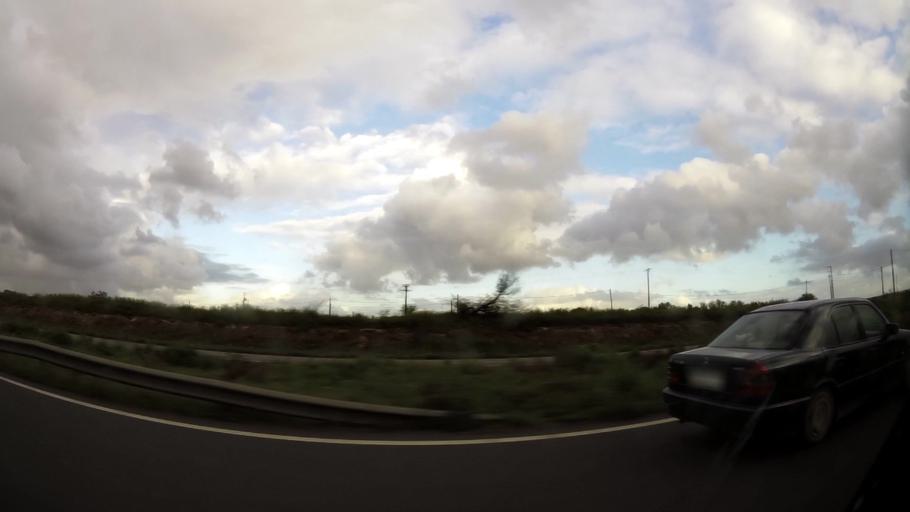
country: MA
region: Grand Casablanca
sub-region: Mohammedia
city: Mohammedia
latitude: 33.6209
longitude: -7.4316
